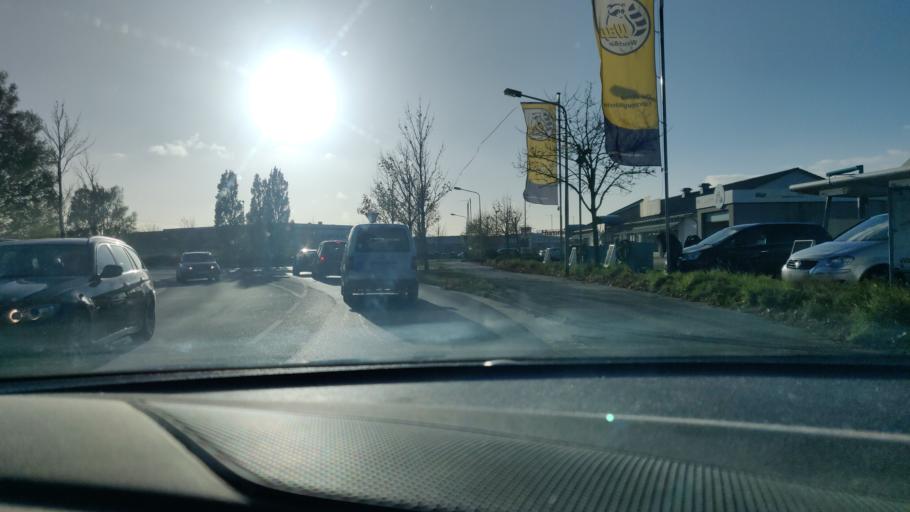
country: DE
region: Lower Saxony
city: Cuxhaven
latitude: 53.8445
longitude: 8.6959
